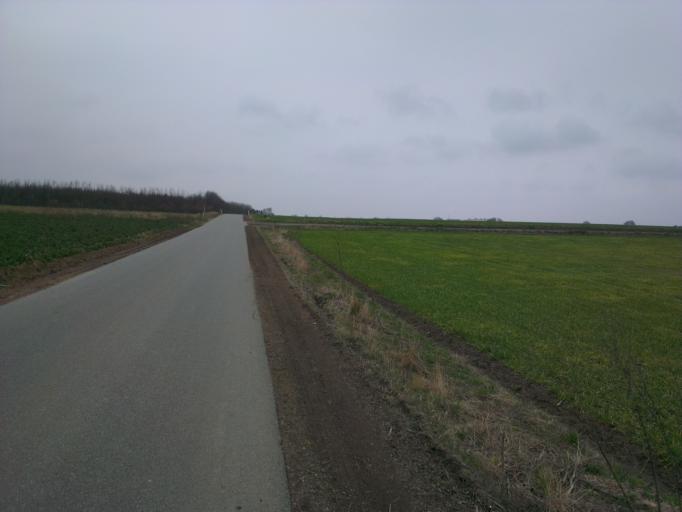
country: DK
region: Capital Region
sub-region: Frederikssund Kommune
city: Frederikssund
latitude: 55.8208
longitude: 12.1121
